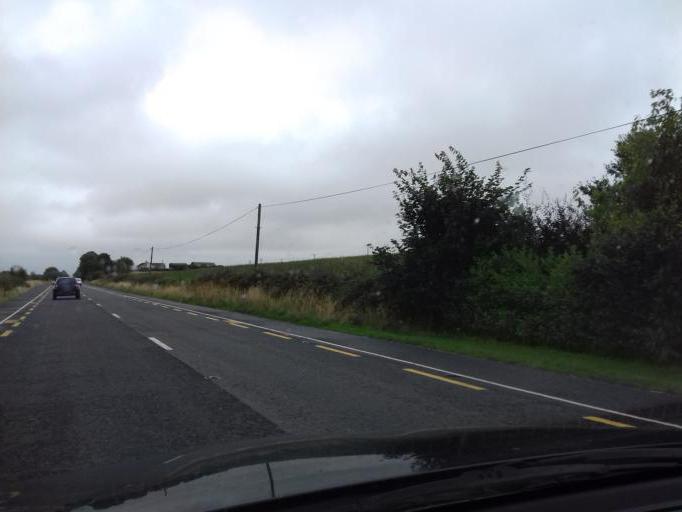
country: IE
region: Leinster
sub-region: County Carlow
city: Bagenalstown
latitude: 52.7505
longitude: -6.9644
